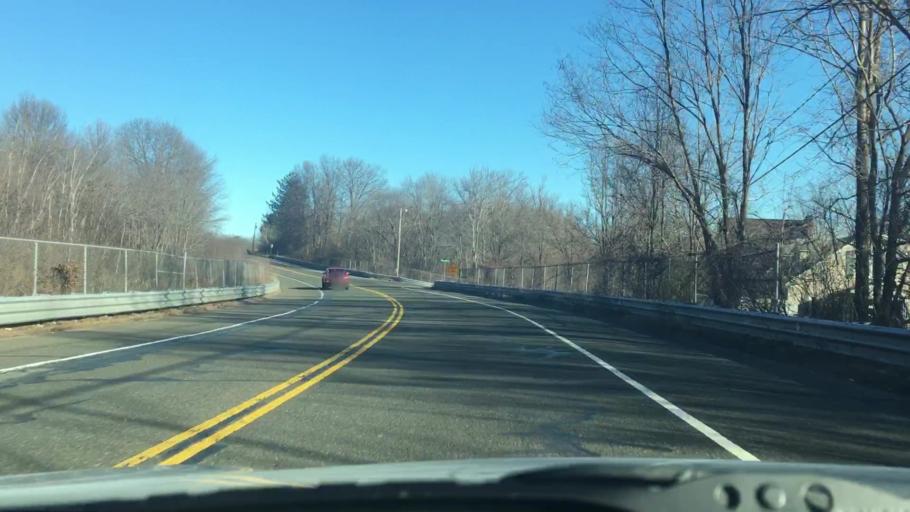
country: US
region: Massachusetts
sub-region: Hampden County
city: Ludlow
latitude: 42.1624
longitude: -72.5157
